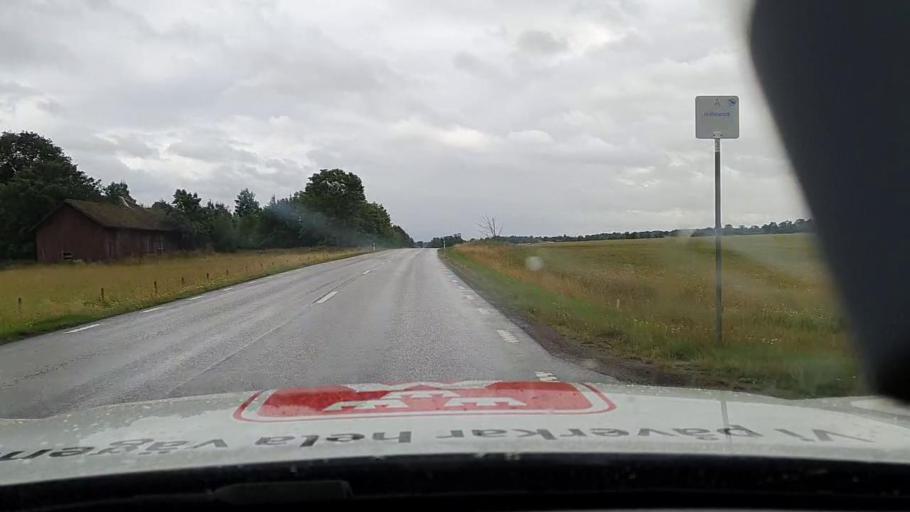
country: SE
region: Vaestra Goetaland
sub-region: Toreboda Kommun
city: Toereboda
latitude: 58.5978
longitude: 14.0097
